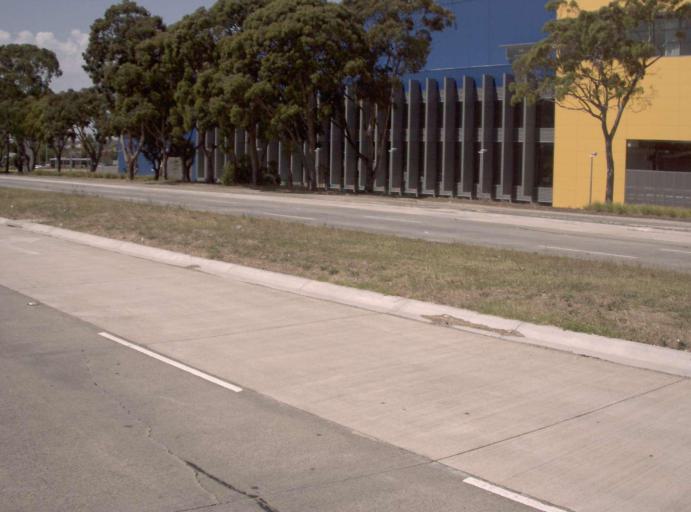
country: AU
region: Victoria
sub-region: Monash
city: Clayton
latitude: -37.9269
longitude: 145.1425
